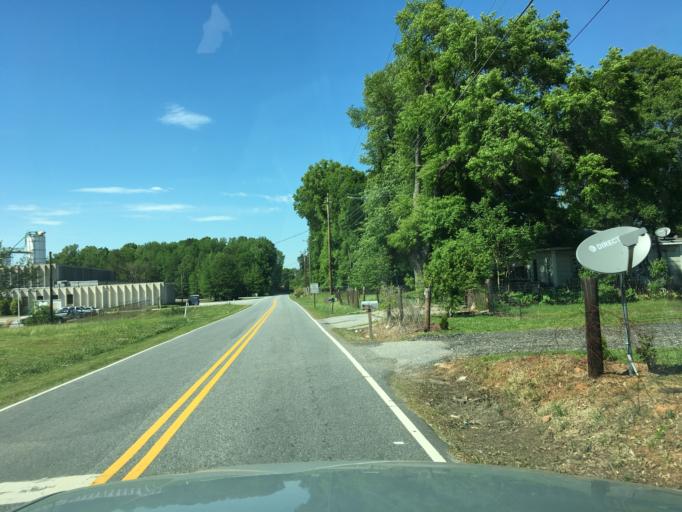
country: US
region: South Carolina
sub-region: Spartanburg County
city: Southern Shops
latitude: 34.9934
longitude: -82.0184
